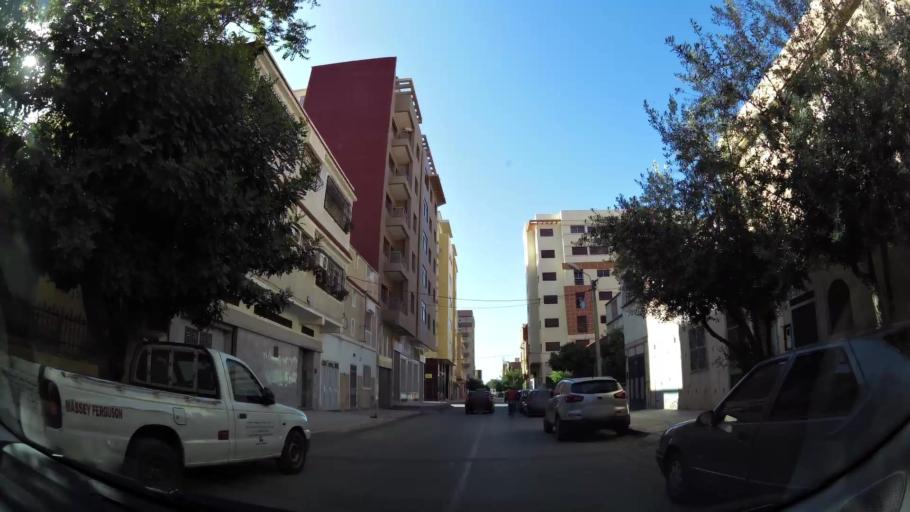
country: MA
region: Oriental
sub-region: Oujda-Angad
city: Oujda
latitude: 34.6873
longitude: -1.9180
